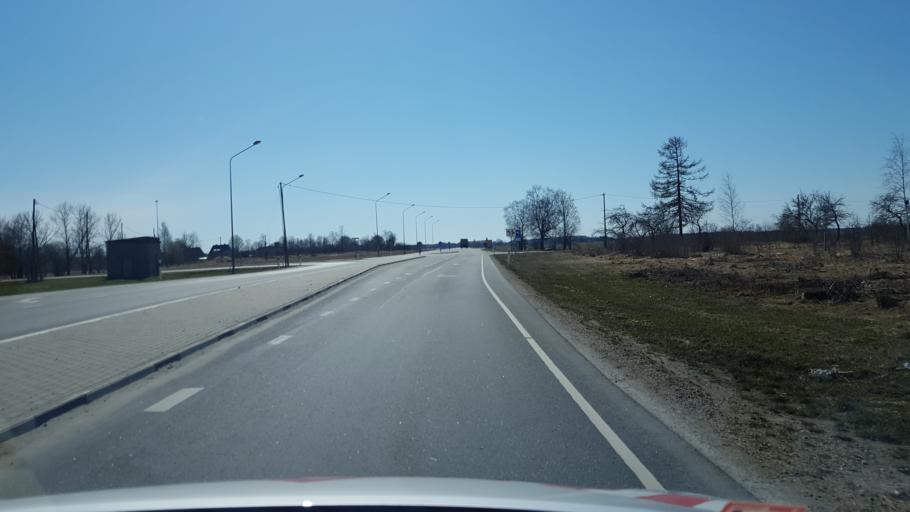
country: EE
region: Ida-Virumaa
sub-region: Johvi vald
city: Johvi
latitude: 59.3307
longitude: 27.4026
